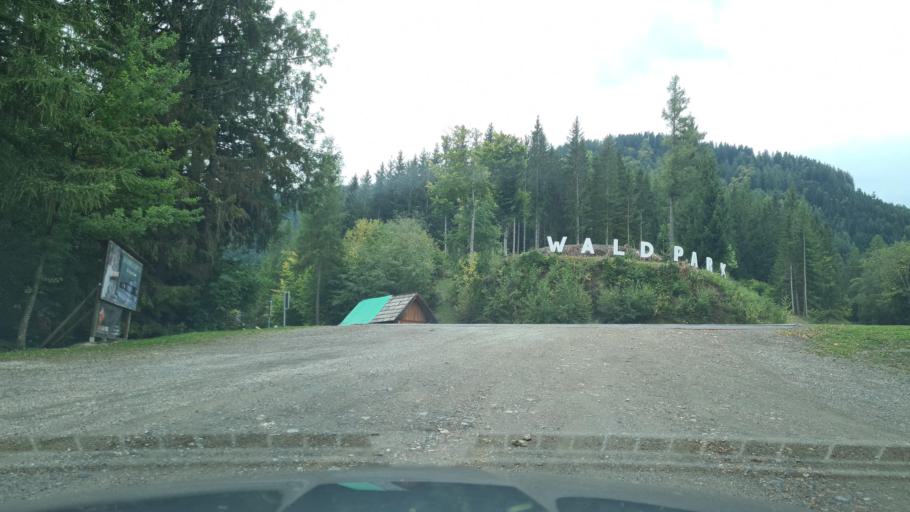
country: AT
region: Styria
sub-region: Politischer Bezirk Weiz
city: Gasen
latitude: 47.3730
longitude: 15.4829
